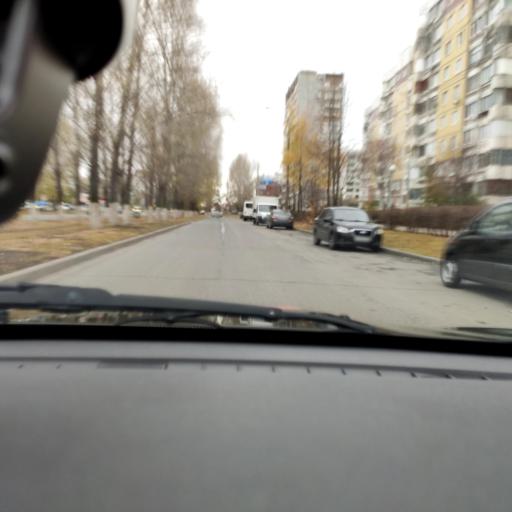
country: RU
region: Samara
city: Tol'yatti
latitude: 53.5385
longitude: 49.3450
